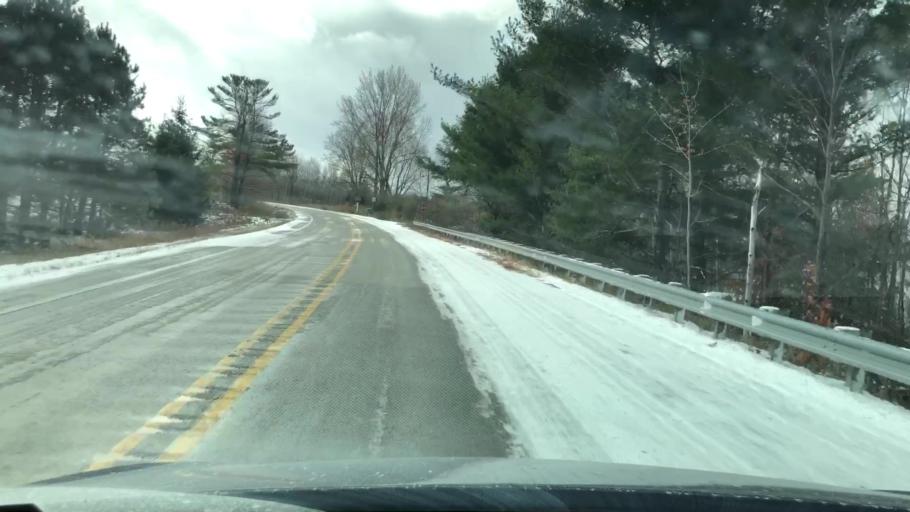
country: US
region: Michigan
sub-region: Antrim County
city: Elk Rapids
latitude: 44.9777
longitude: -85.5040
